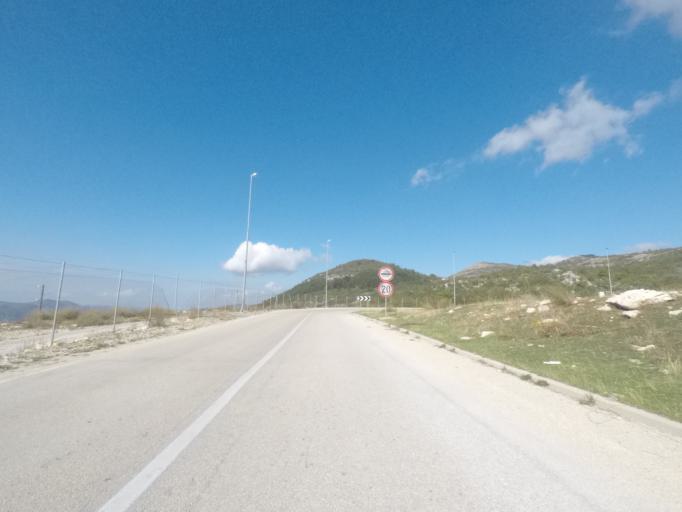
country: BA
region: Republika Srpska
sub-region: Opstina Bileca
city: Bileca
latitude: 42.7126
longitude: 18.5476
